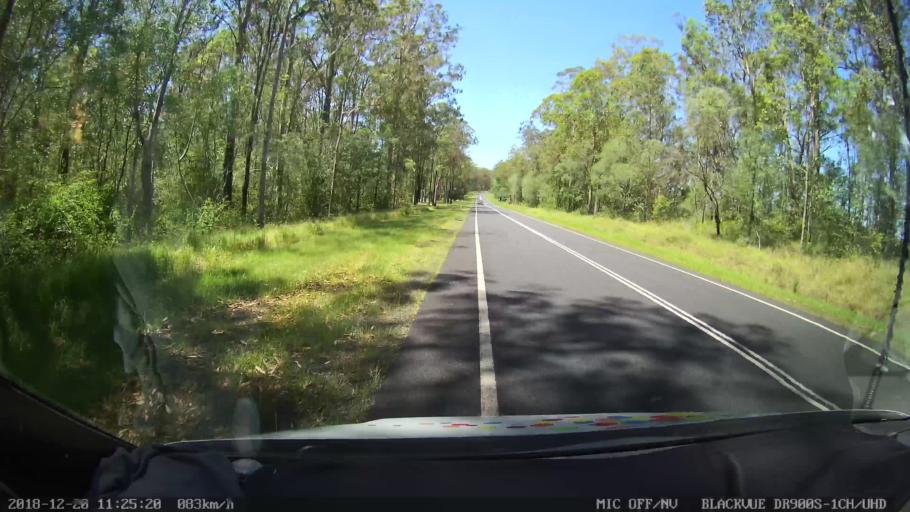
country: AU
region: New South Wales
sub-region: Richmond Valley
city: Casino
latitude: -29.0862
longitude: 153.0009
